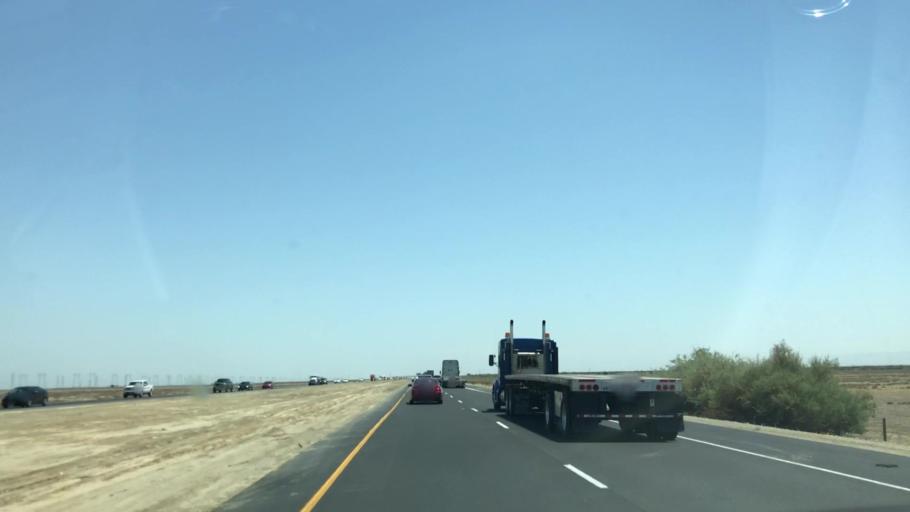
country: US
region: California
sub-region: Kern County
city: Lost Hills
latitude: 35.8162
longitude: -119.8024
